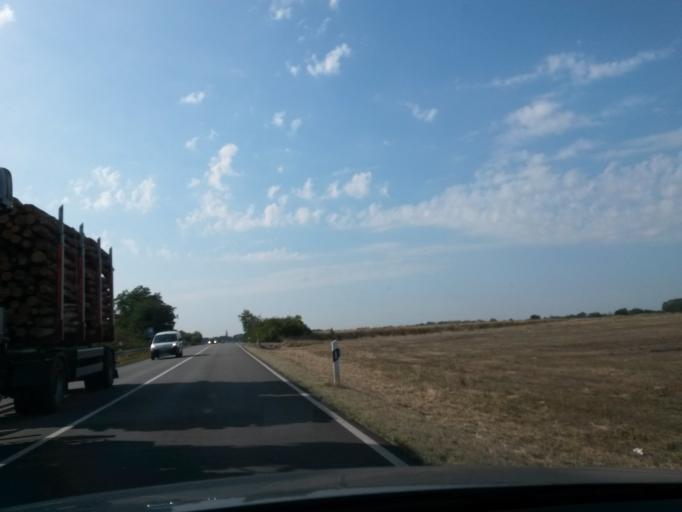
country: DE
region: Saxony-Anhalt
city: Jerichow
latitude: 52.5262
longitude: 12.0158
